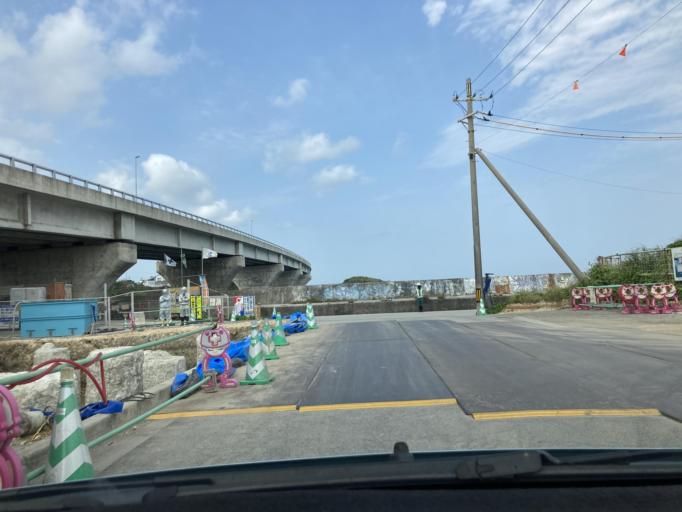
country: JP
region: Okinawa
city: Ginowan
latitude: 26.2738
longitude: 127.7130
